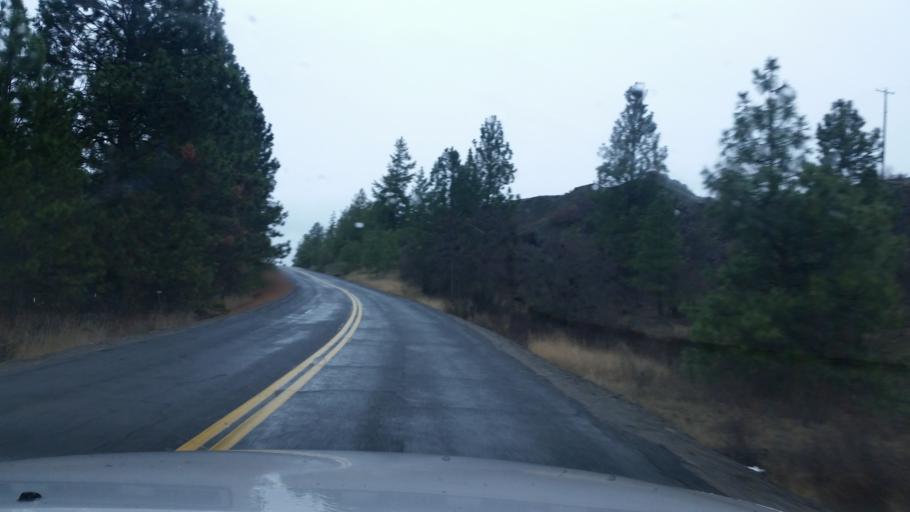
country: US
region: Washington
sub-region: Spokane County
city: Airway Heights
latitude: 47.6978
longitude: -117.5724
